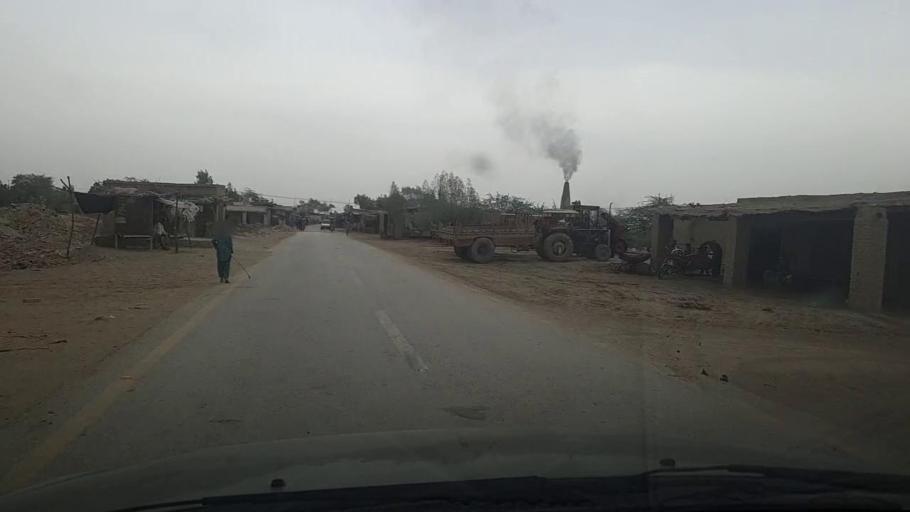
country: PK
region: Sindh
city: Daulatpur
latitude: 26.3412
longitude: 68.1238
